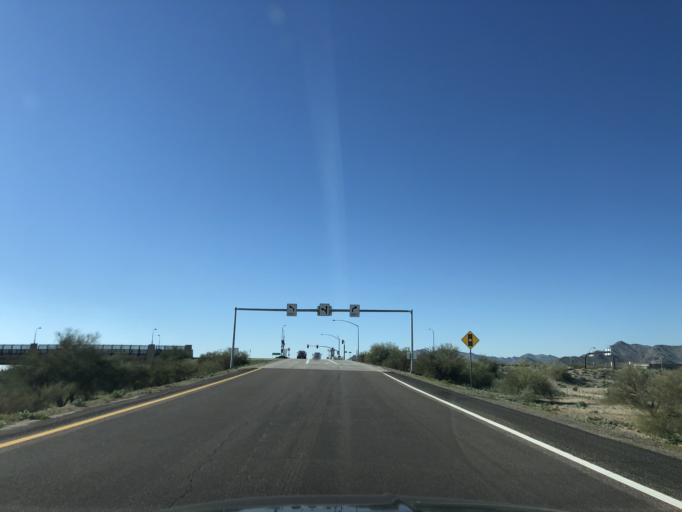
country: US
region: Arizona
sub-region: Maricopa County
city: Citrus Park
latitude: 33.4623
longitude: -112.5021
